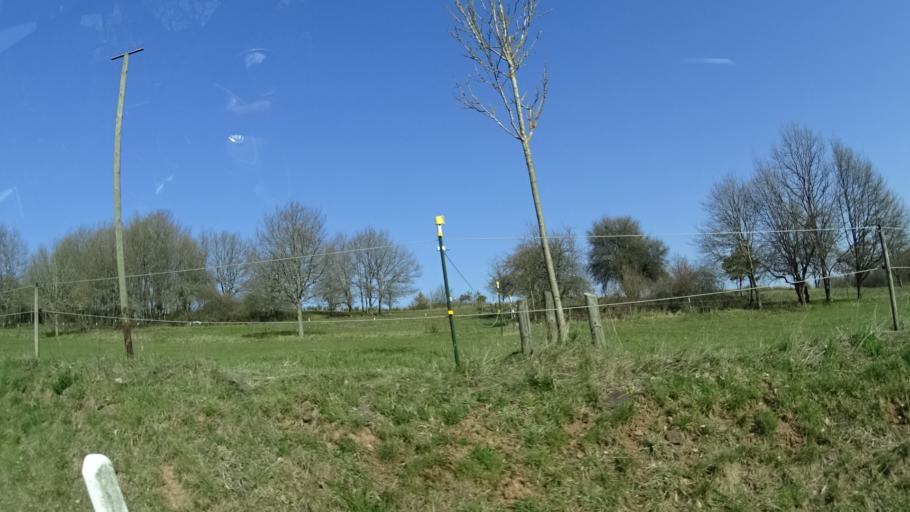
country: DE
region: Rheinland-Pfalz
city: Frauenberg
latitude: 49.6733
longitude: 7.2786
